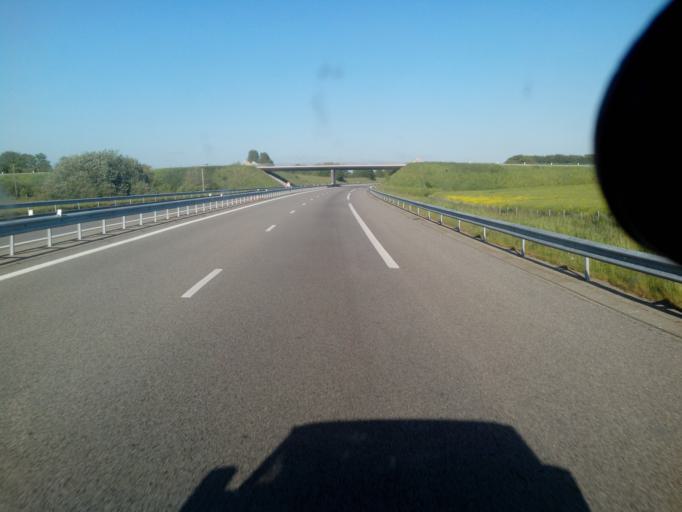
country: FR
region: Haute-Normandie
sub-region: Departement de la Seine-Maritime
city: Nointot
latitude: 49.6042
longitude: 0.4733
